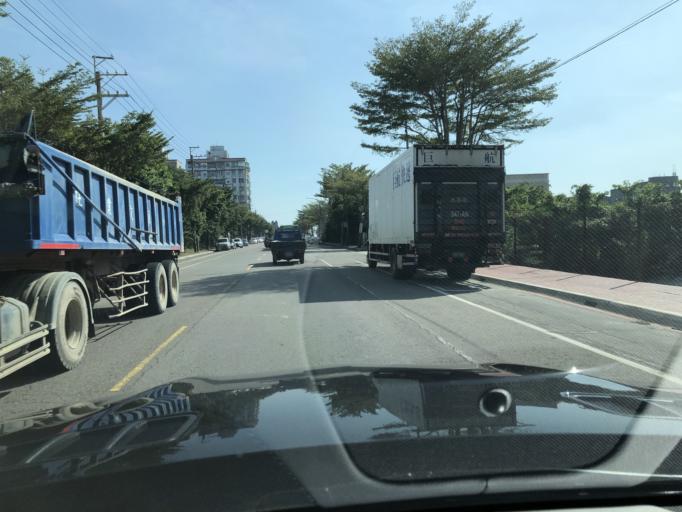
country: TW
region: Taiwan
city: Taoyuan City
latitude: 25.0689
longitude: 121.2894
